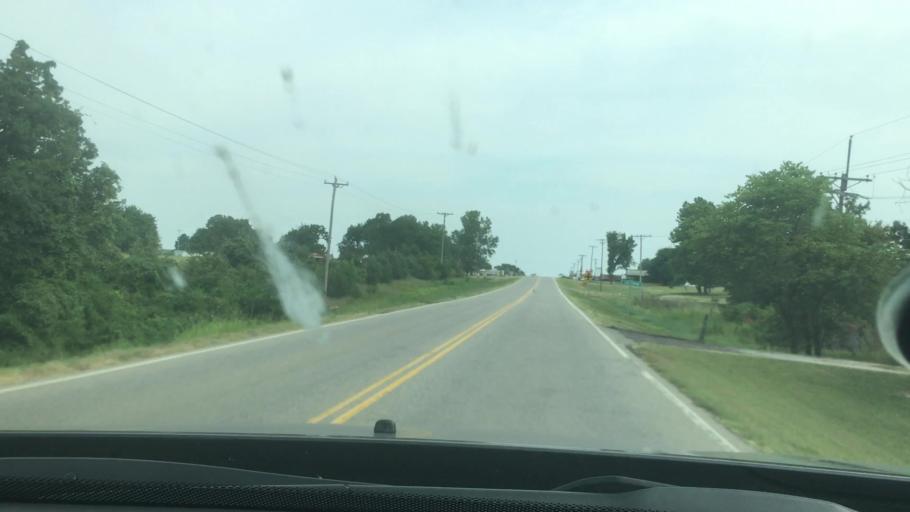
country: US
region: Oklahoma
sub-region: Johnston County
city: Tishomingo
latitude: 34.2690
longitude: -96.4248
